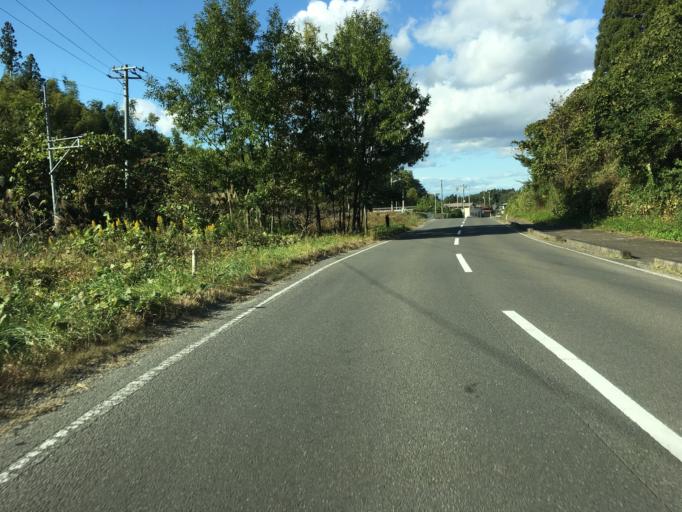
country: JP
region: Miyagi
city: Marumori
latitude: 37.8610
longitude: 140.8273
